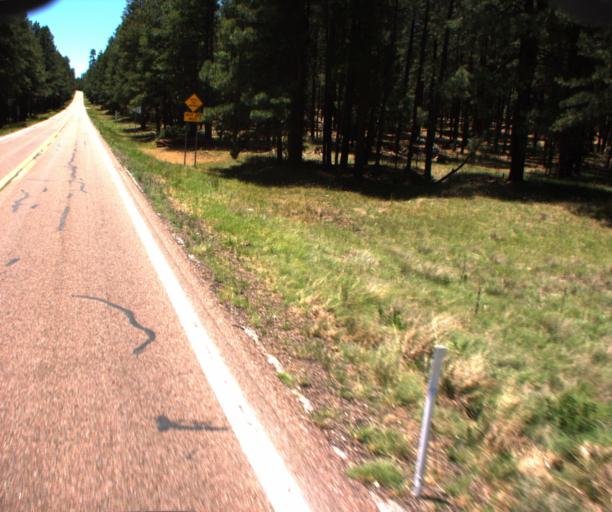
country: US
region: Arizona
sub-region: Gila County
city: Pine
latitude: 34.5267
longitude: -111.3419
